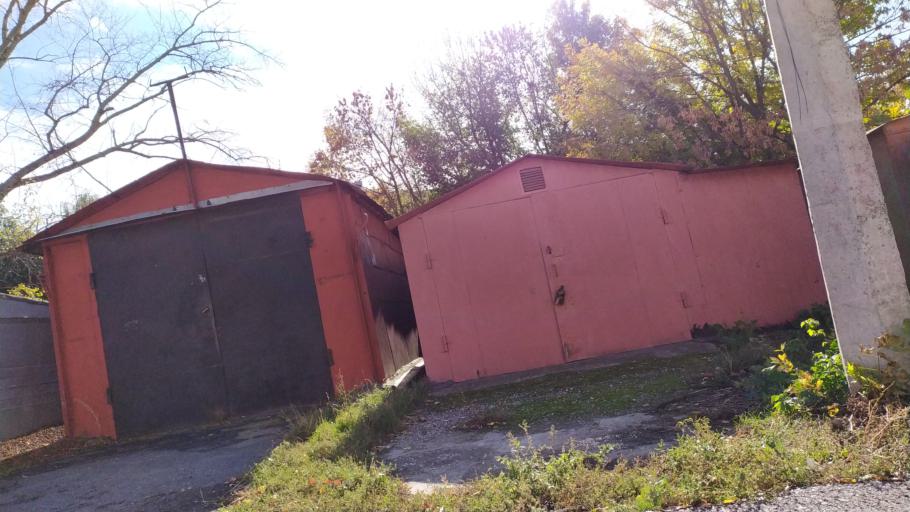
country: RU
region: Kursk
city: Kursk
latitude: 51.6514
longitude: 36.1413
